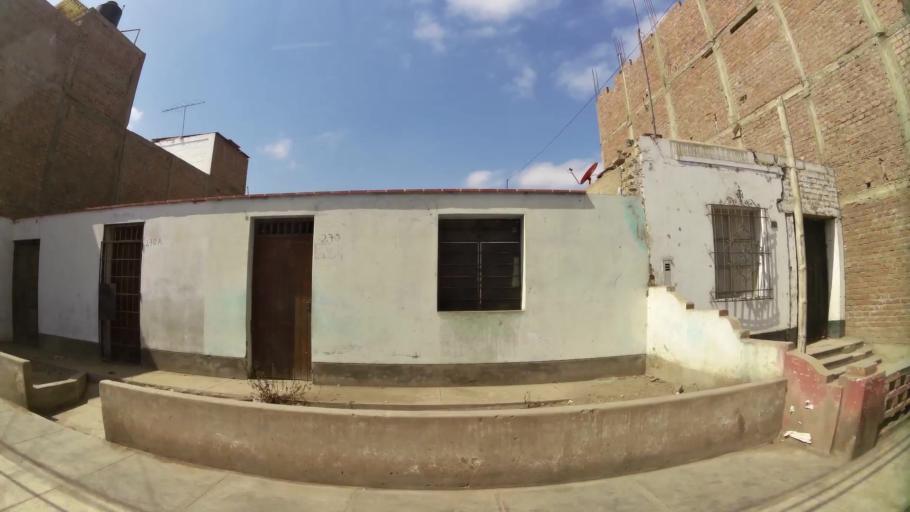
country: PE
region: Lima
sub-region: Provincia de Canete
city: Mala
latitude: -12.6559
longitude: -76.6322
